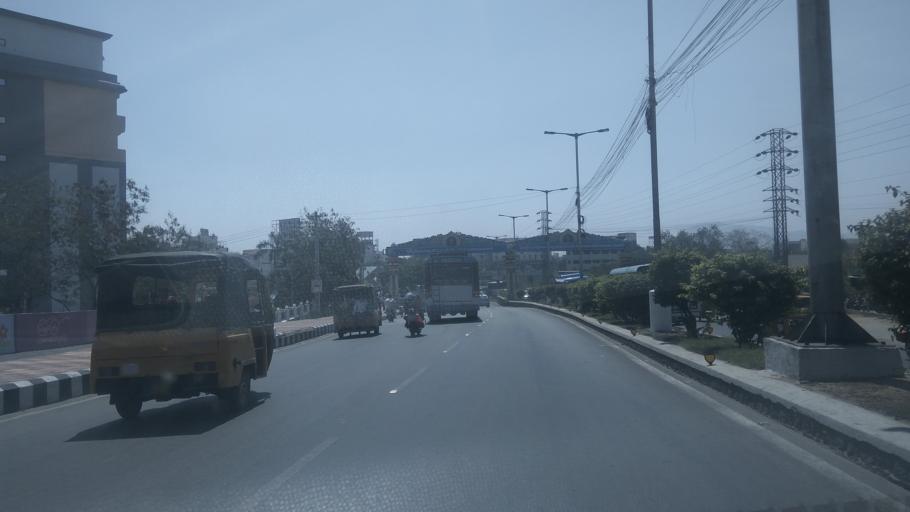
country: IN
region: Andhra Pradesh
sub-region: Chittoor
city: Tirupati
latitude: 13.6278
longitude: 79.4296
